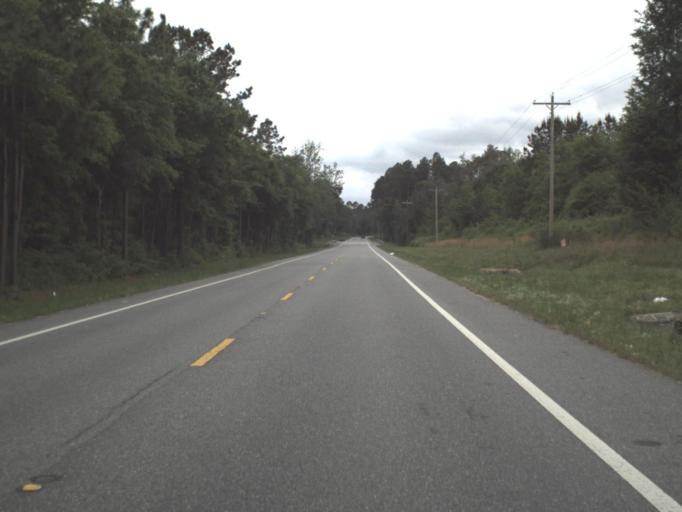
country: US
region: Florida
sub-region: Santa Rosa County
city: Point Baker
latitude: 30.8048
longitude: -87.0428
